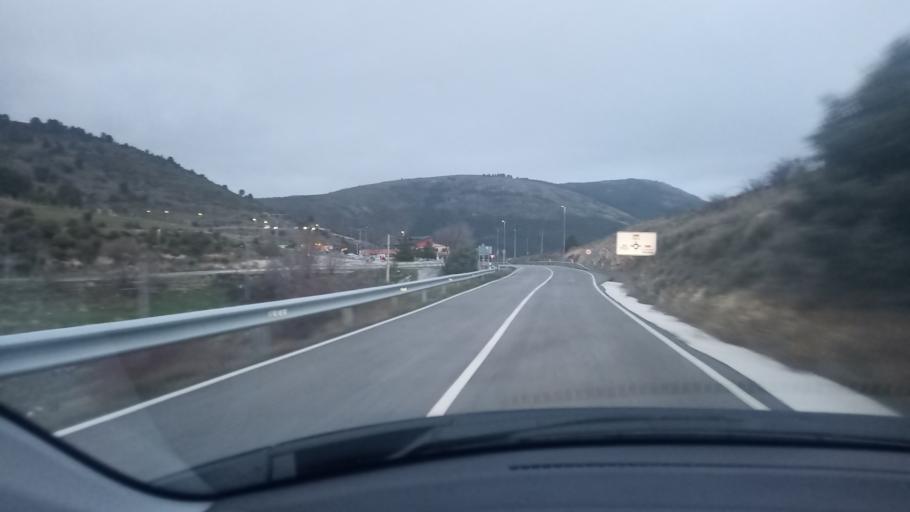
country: ES
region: Madrid
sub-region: Provincia de Madrid
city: Zarzalejo
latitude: 40.5574
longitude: -4.1965
